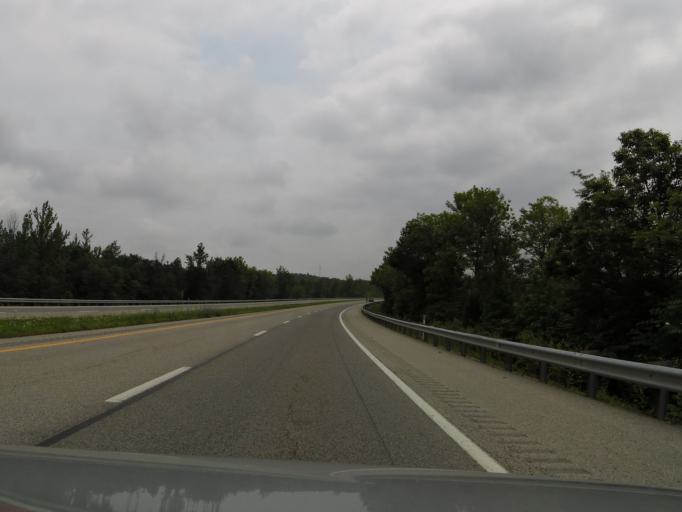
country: US
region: Kentucky
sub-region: Ohio County
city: Beaver Dam
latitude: 37.3303
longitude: -86.9845
